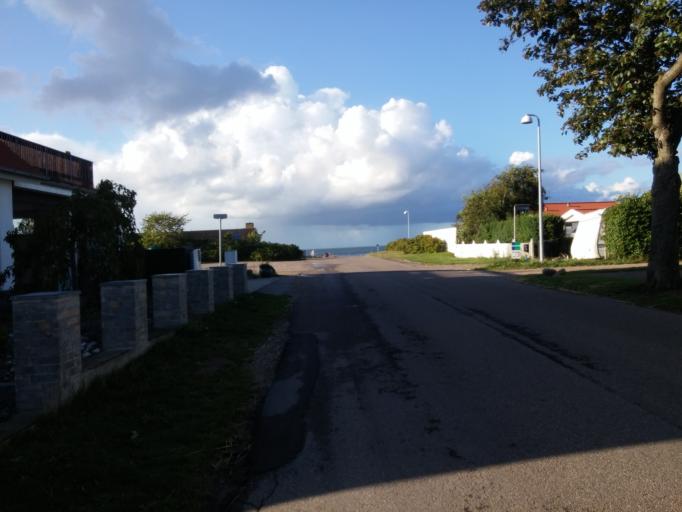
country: DK
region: Zealand
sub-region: Kalundborg Kommune
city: Svebolle
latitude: 55.7533
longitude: 11.3383
